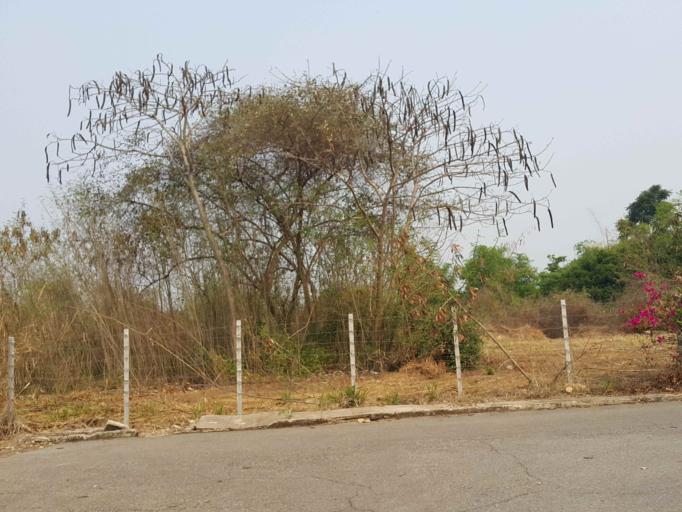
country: TH
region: Chiang Mai
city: Saraphi
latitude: 18.7578
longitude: 99.0577
